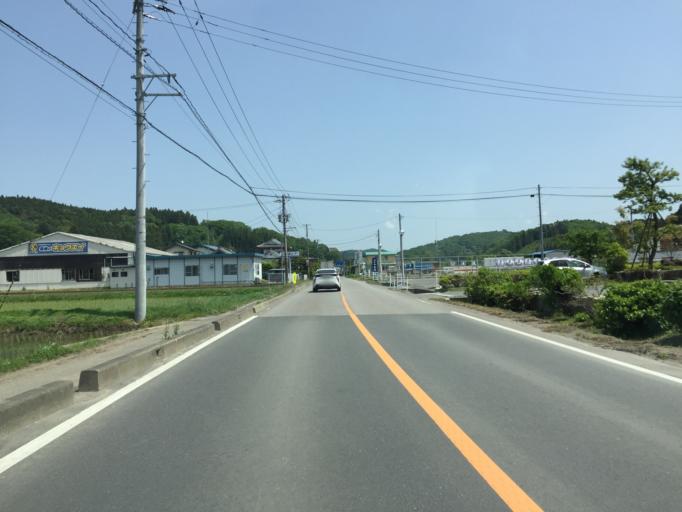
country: JP
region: Fukushima
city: Ishikawa
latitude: 37.1421
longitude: 140.4160
